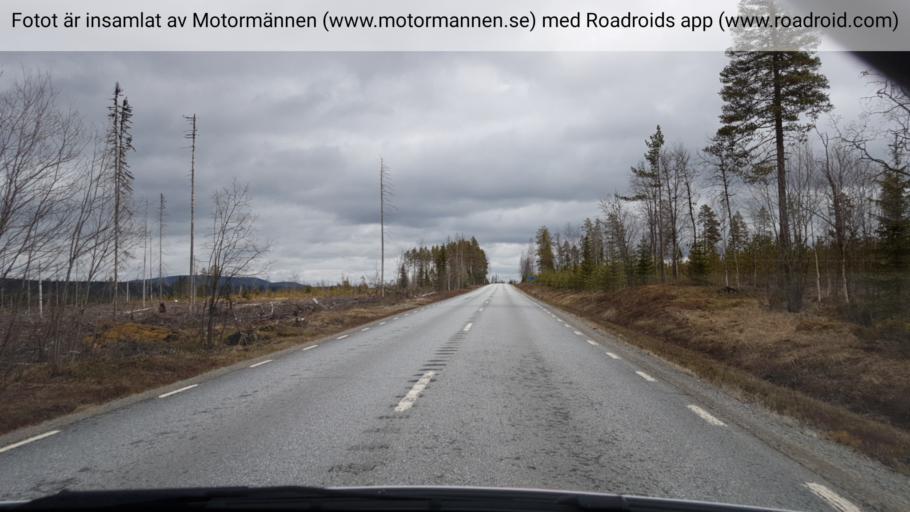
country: SE
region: Vaesterbotten
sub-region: Bjurholms Kommun
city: Bjurholm
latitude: 63.9561
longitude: 18.8750
